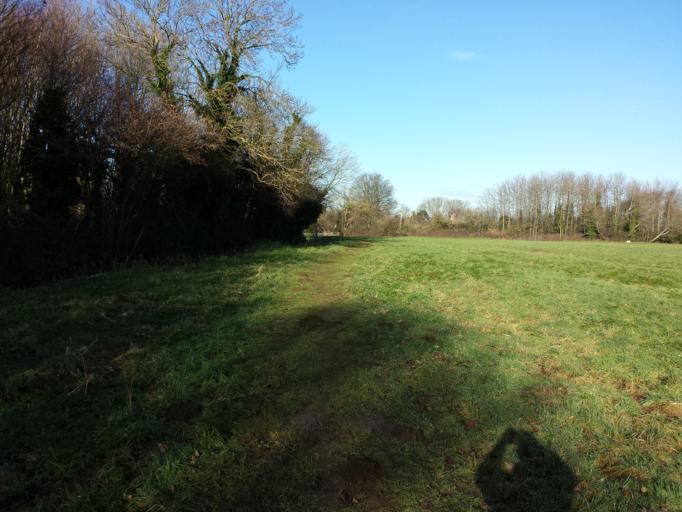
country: GB
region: England
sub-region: Worcestershire
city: Broadway
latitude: 52.0432
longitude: -1.8904
